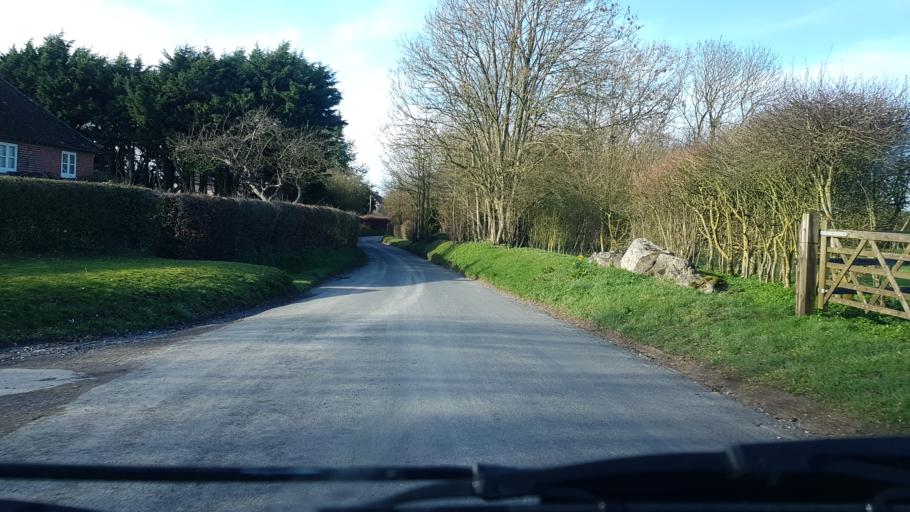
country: GB
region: England
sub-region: Wiltshire
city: Avebury
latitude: 51.4032
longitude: -1.8278
